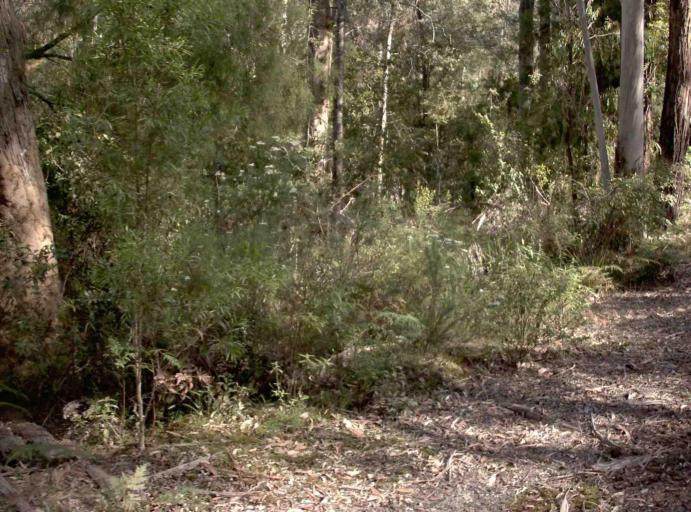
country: AU
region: Victoria
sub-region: East Gippsland
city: Lakes Entrance
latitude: -37.4642
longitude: 148.5644
